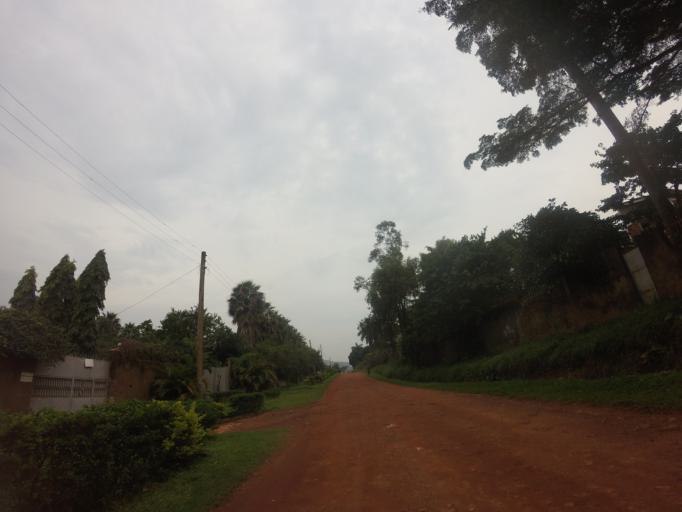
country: UG
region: Central Region
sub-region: Wakiso District
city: Kireka
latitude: 0.3531
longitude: 32.6220
